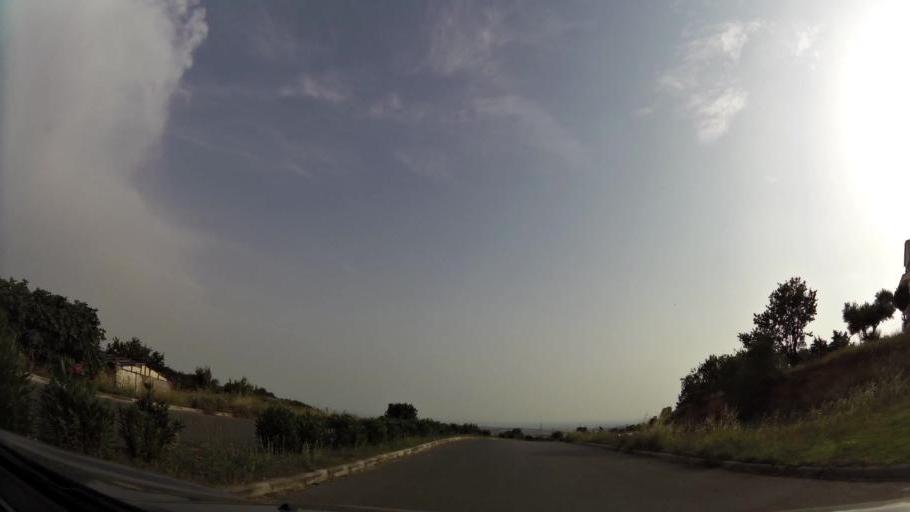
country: GR
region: Central Macedonia
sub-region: Nomos Thessalonikis
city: Oraiokastro
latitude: 40.7203
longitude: 22.9179
